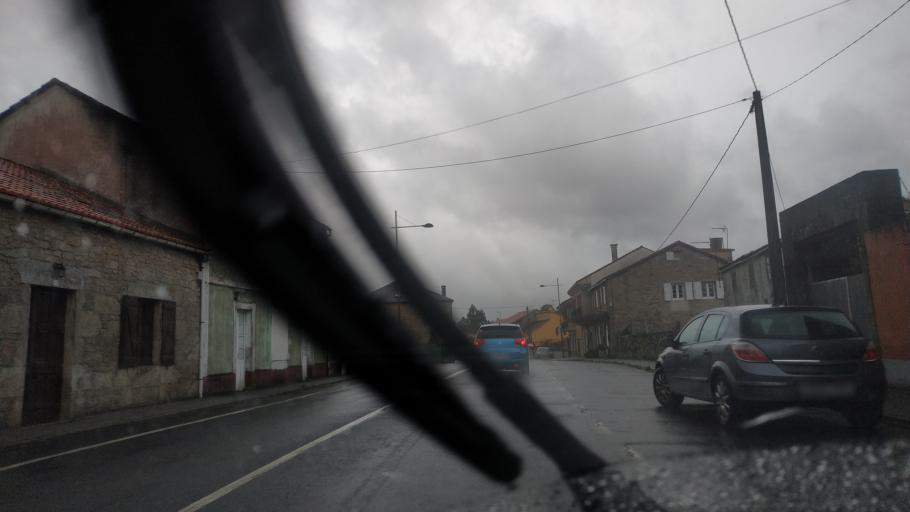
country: ES
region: Galicia
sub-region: Provincia da Coruna
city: Negreira
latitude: 42.9230
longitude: -8.7342
